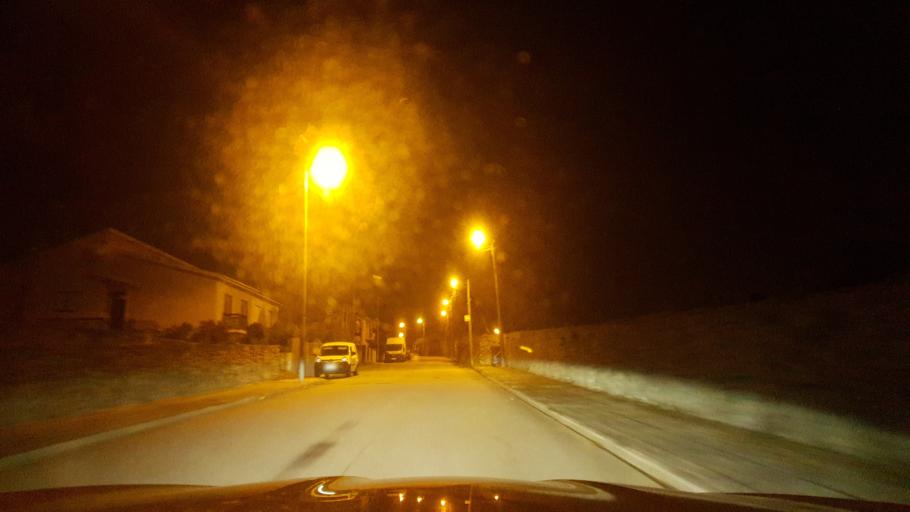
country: PT
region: Porto
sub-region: Matosinhos
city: Guifoes
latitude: 41.2155
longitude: -8.6452
